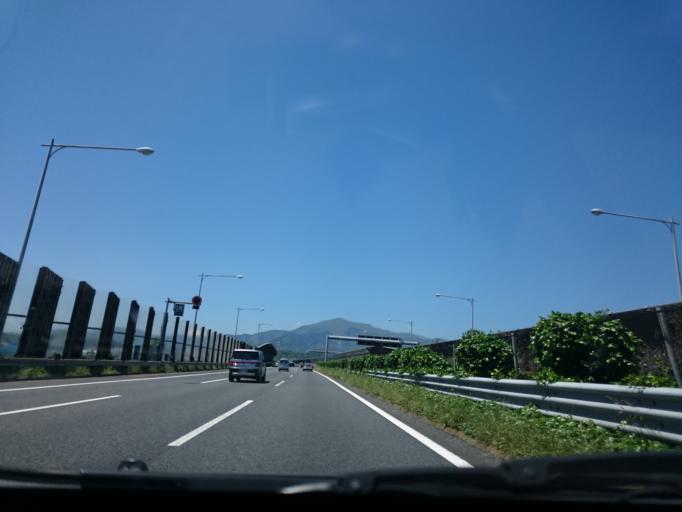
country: JP
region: Kanagawa
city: Atsugi
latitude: 35.4248
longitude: 139.3550
